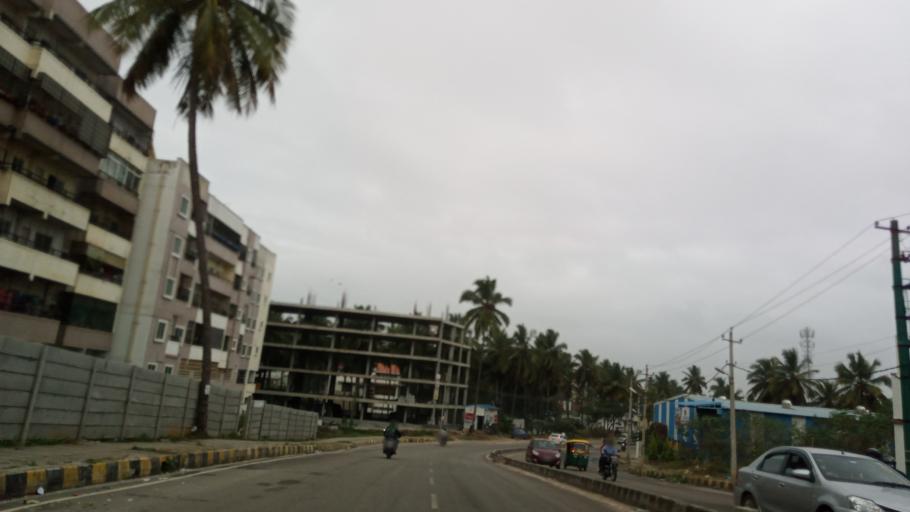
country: IN
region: Karnataka
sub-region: Bangalore Urban
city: Bangalore
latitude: 12.9077
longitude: 77.4884
